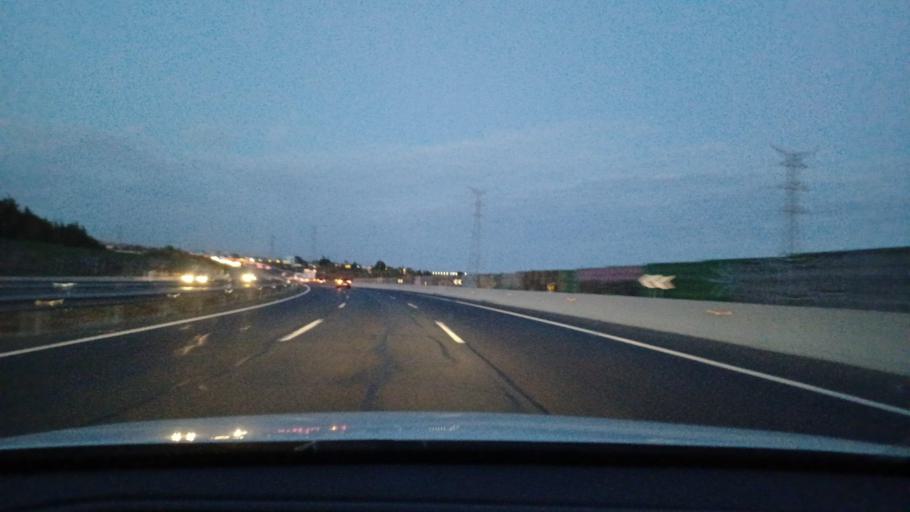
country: ES
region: Valencia
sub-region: Provincia de Alicante
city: Crevillente
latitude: 38.2433
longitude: -0.7768
